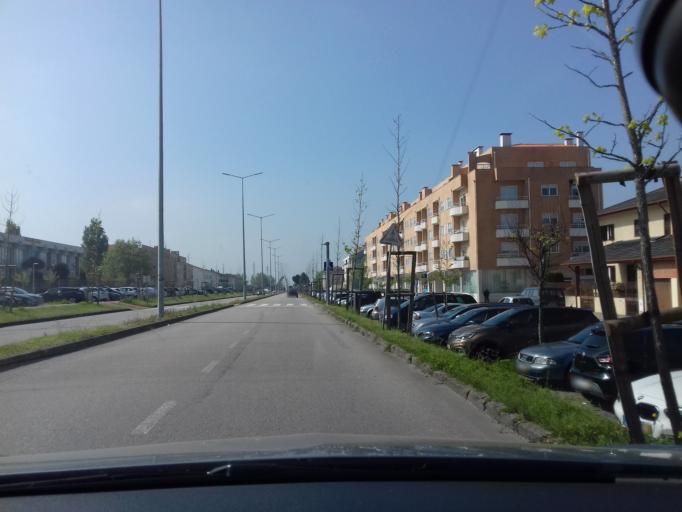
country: PT
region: Aveiro
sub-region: Espinho
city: Espinho
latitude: 41.0071
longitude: -8.6343
